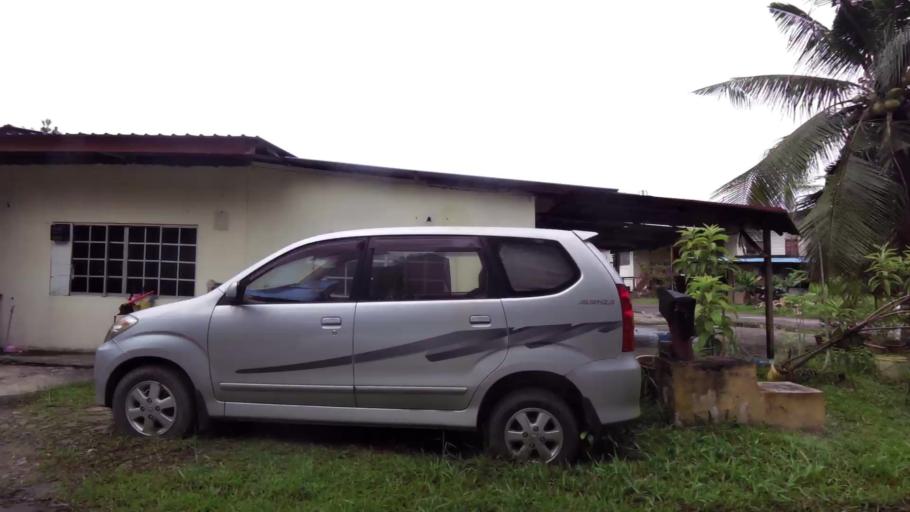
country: BN
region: Brunei and Muara
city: Bandar Seri Begawan
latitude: 4.8977
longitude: 114.9309
